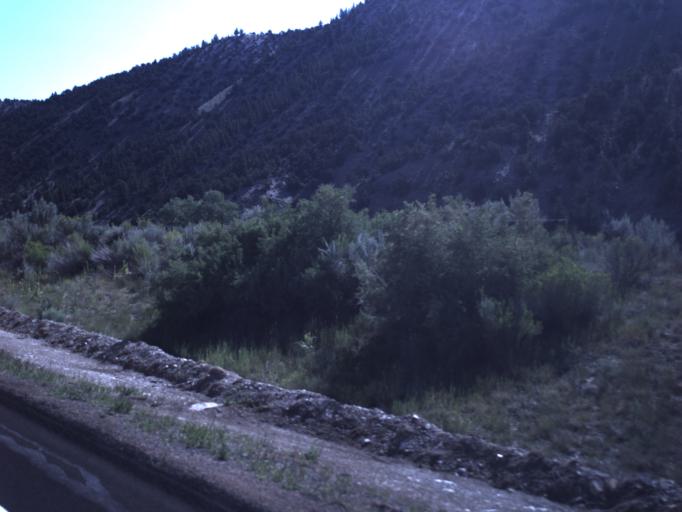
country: US
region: Utah
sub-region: Duchesne County
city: Duchesne
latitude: 40.0092
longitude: -110.5695
